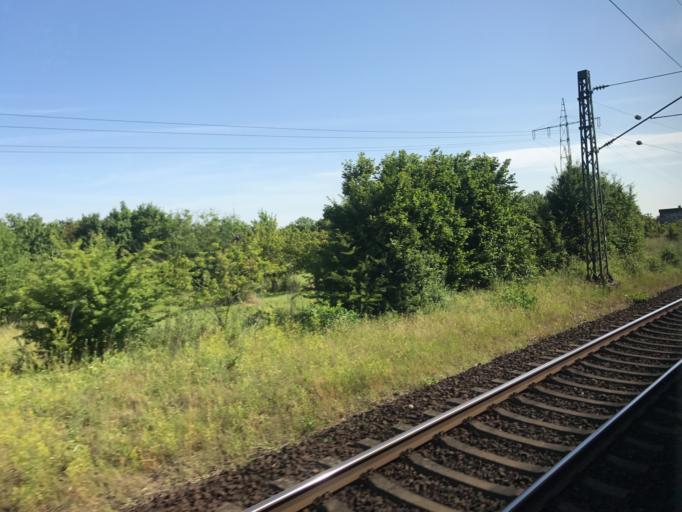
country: DE
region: Rheinland-Pfalz
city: Nieder-Ingelheim
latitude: 49.9920
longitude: 8.0789
